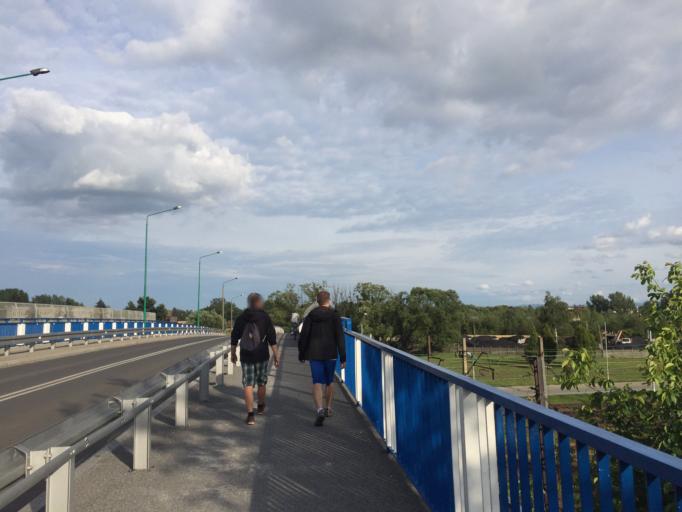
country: PL
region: Lesser Poland Voivodeship
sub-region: Powiat oswiecimski
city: Brzezinka
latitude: 50.0364
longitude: 19.1925
